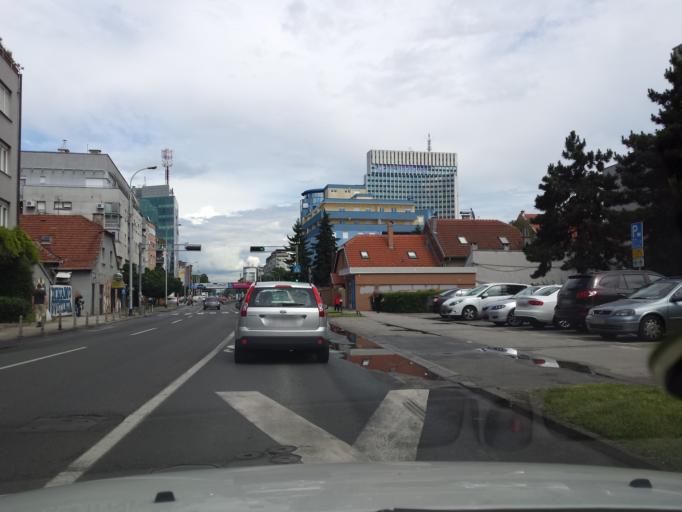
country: HR
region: Grad Zagreb
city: Zagreb - Centar
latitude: 45.7993
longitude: 15.9576
